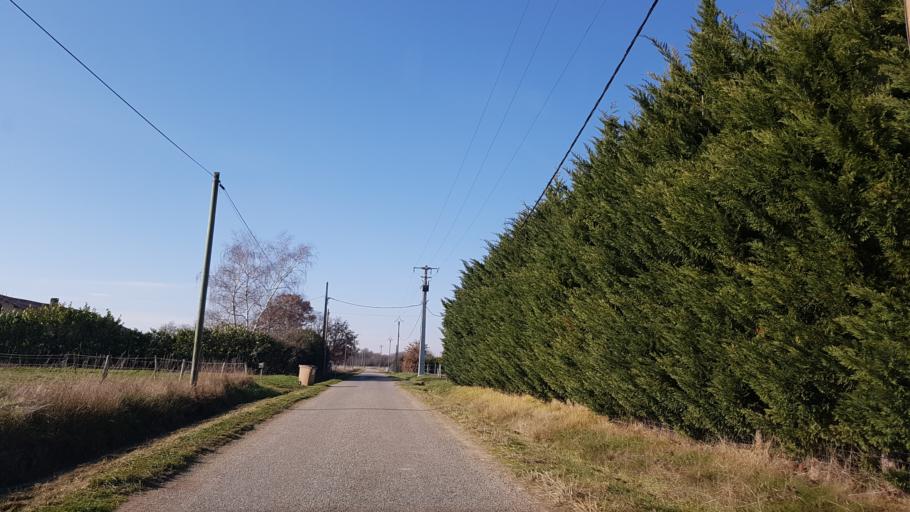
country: FR
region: Midi-Pyrenees
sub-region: Departement de l'Ariege
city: La Tour-du-Crieu
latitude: 43.1630
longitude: 1.6786
